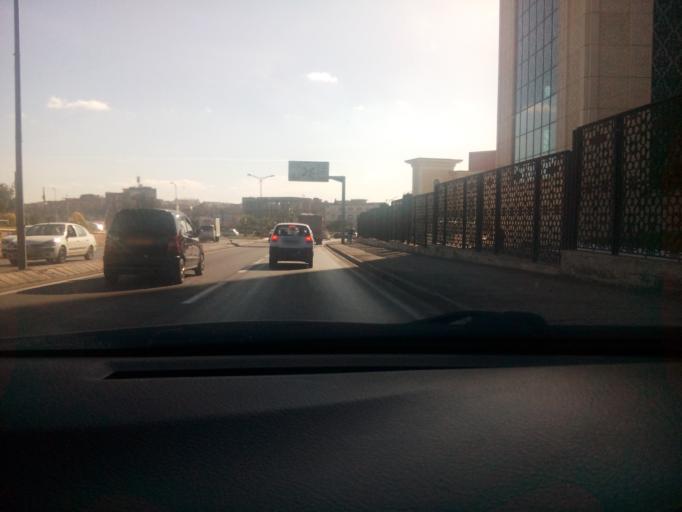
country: DZ
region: Oran
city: Oran
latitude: 35.6984
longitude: -0.6057
